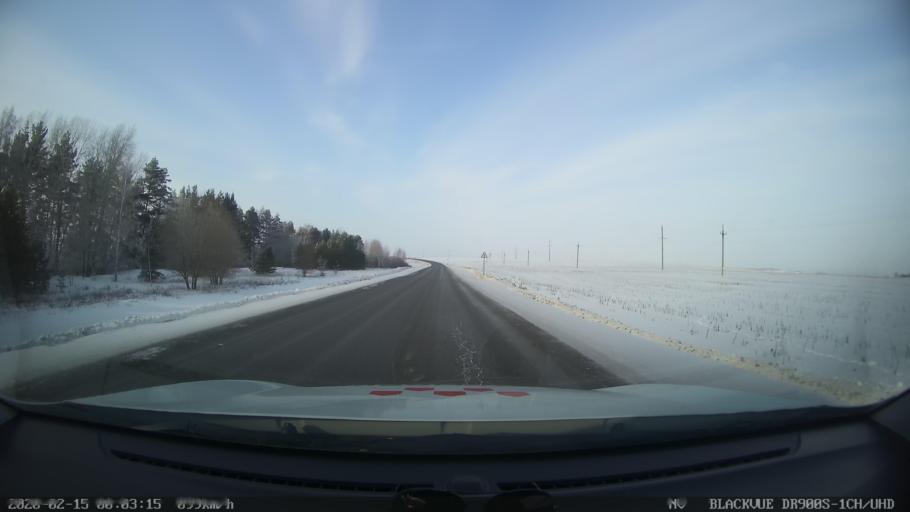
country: RU
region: Tatarstan
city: Kuybyshevskiy Zaton
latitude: 55.3694
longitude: 48.9989
